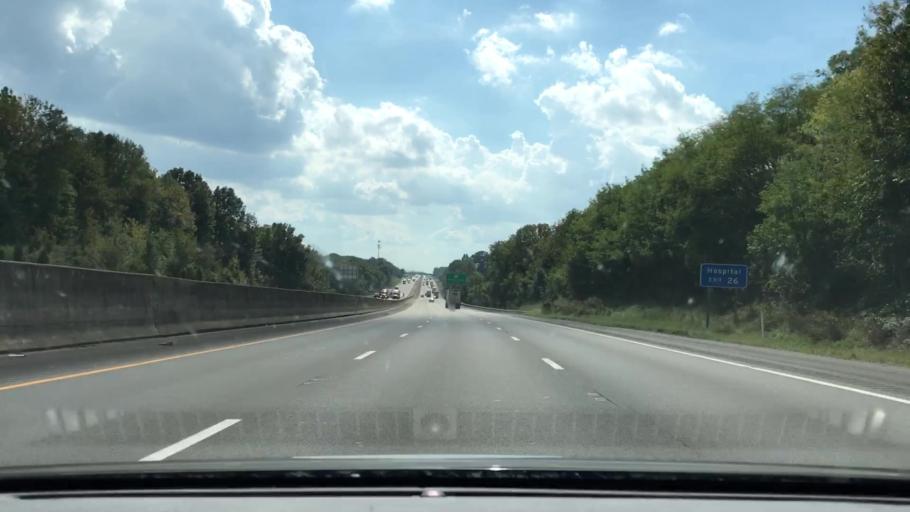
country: US
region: Kentucky
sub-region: Warren County
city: Bowling Green
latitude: 36.9915
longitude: -86.3837
